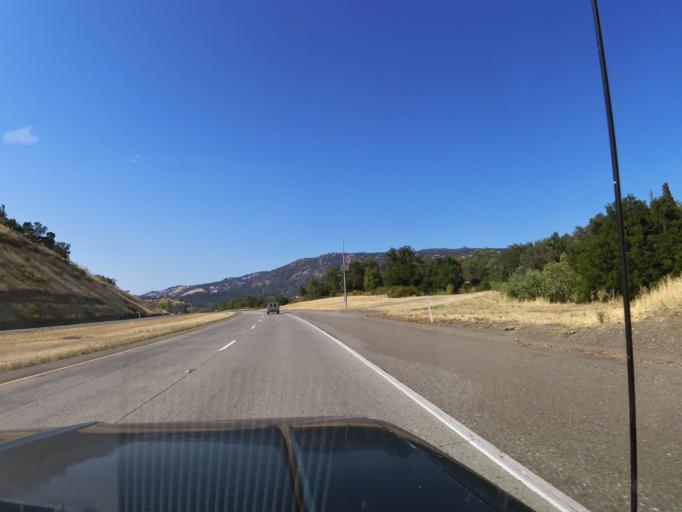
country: US
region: California
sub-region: Sonoma County
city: Cloverdale
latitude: 38.8087
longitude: -123.0117
